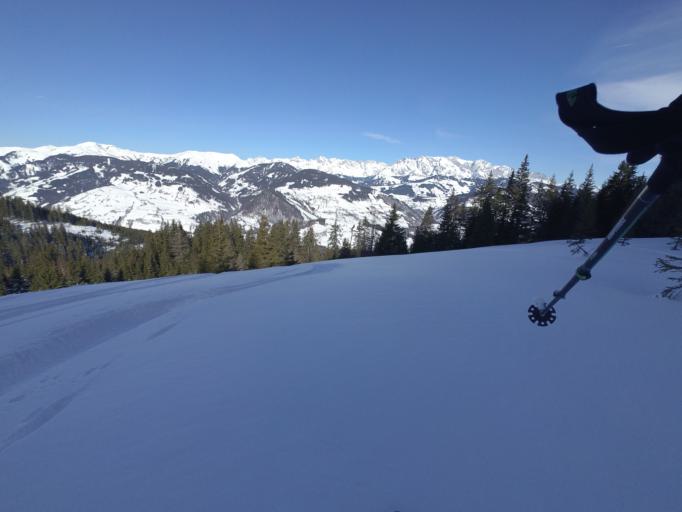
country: AT
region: Salzburg
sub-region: Politischer Bezirk Zell am See
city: Lend
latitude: 47.2725
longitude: 13.0182
